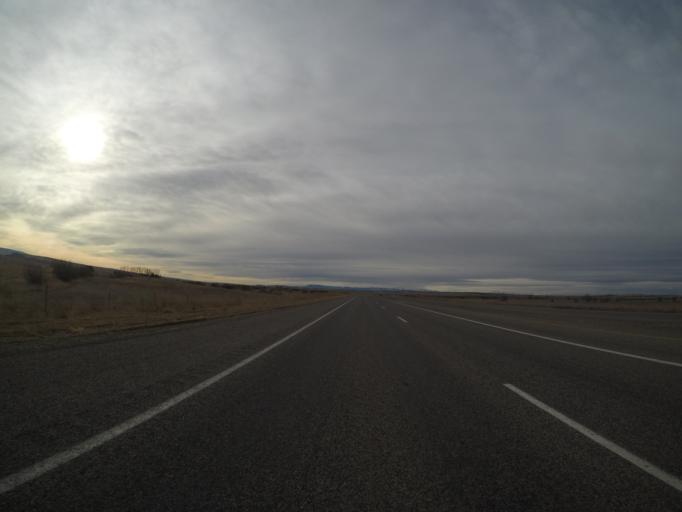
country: US
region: Montana
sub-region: Yellowstone County
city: Laurel
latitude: 45.5951
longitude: -108.8280
